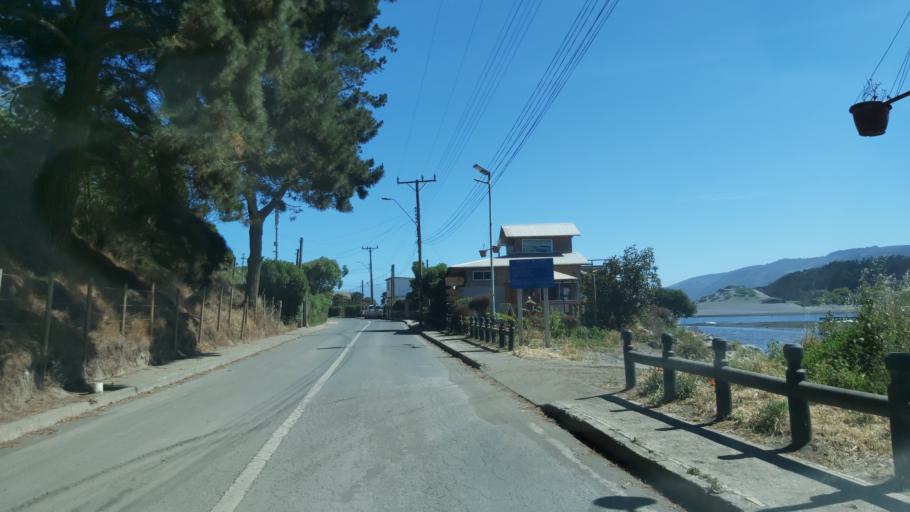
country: CL
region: Maule
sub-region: Provincia de Talca
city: Constitucion
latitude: -34.7561
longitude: -72.0836
